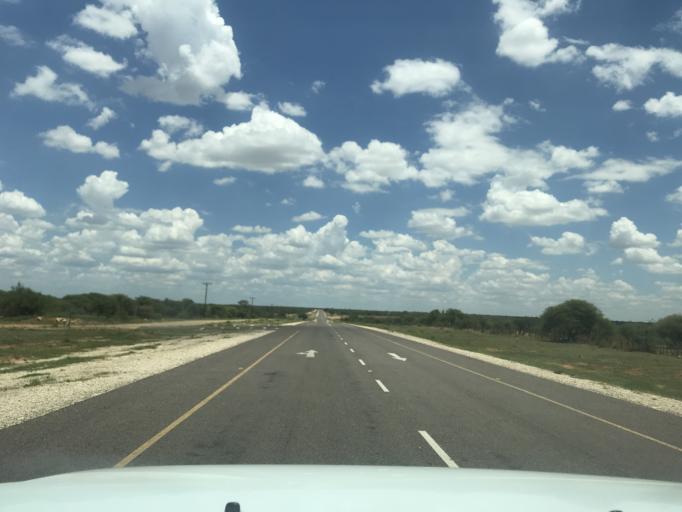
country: BW
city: Mabuli
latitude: -25.7142
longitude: 25.0633
